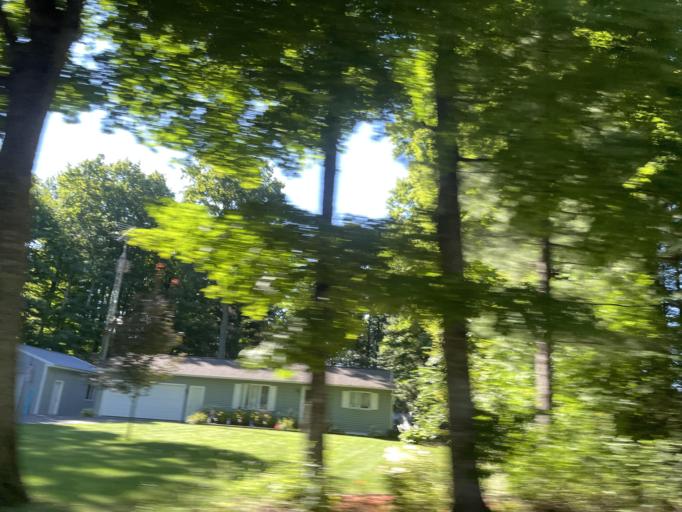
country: US
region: Michigan
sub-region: Benzie County
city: Beulah
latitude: 44.6173
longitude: -86.0620
